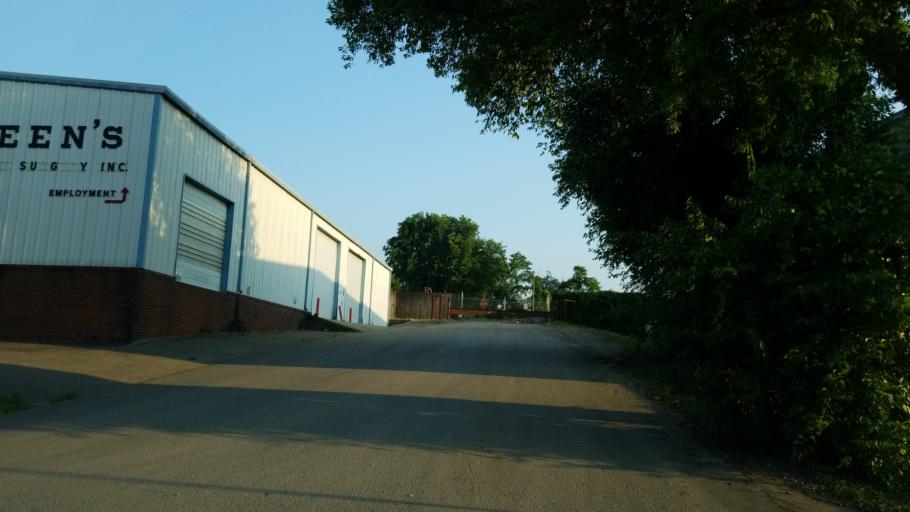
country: US
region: Tennessee
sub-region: Davidson County
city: Nashville
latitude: 36.1389
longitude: -86.7721
